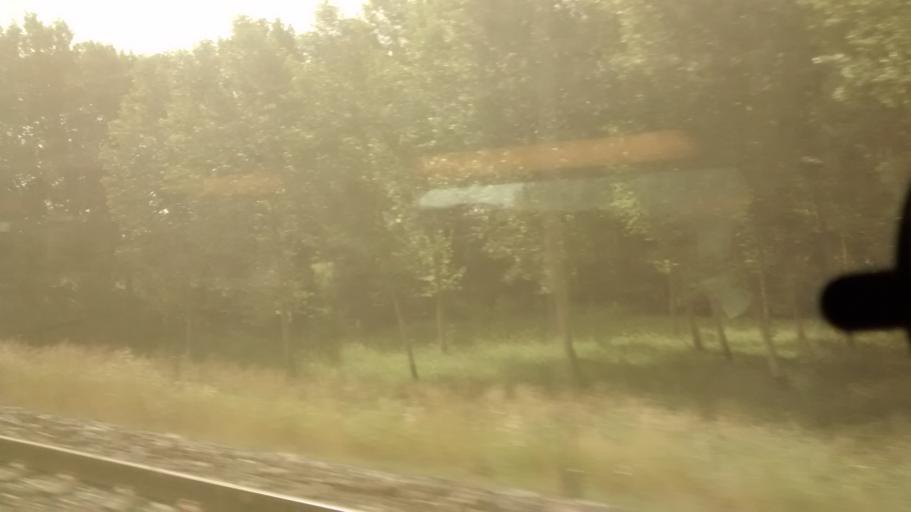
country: FR
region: Pays de la Loire
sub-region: Departement de la Sarthe
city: Vibraye
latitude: 48.0828
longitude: 0.7302
